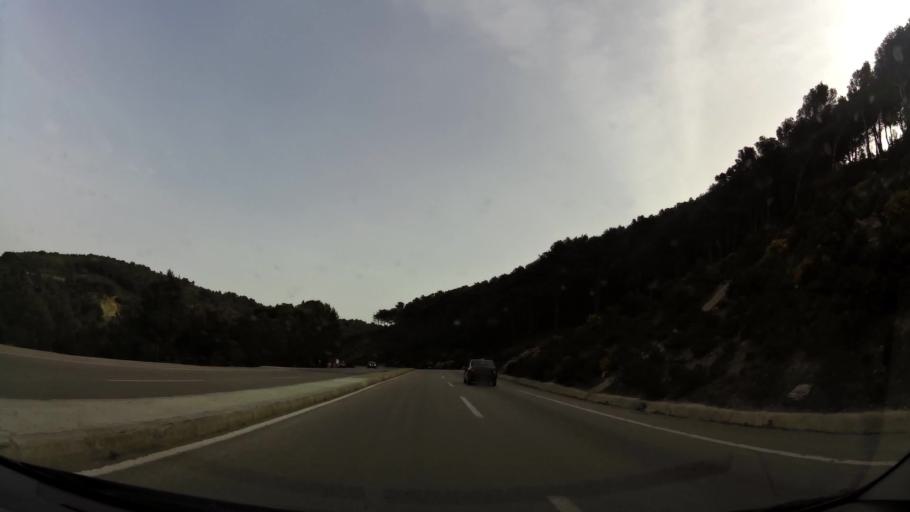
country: MA
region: Tanger-Tetouan
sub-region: Tanger-Assilah
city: Dar Chaoui
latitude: 35.5630
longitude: -5.5851
